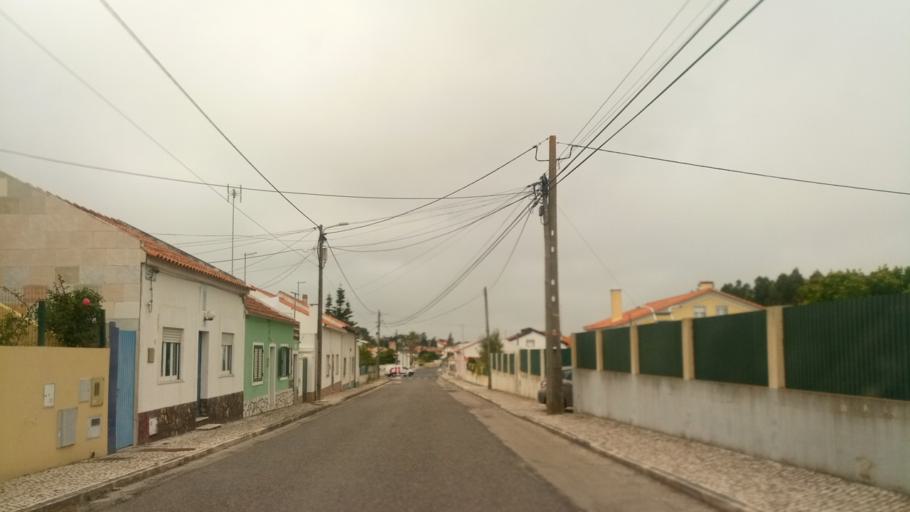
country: PT
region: Leiria
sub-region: Caldas da Rainha
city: Caldas da Rainha
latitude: 39.4308
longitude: -9.1541
